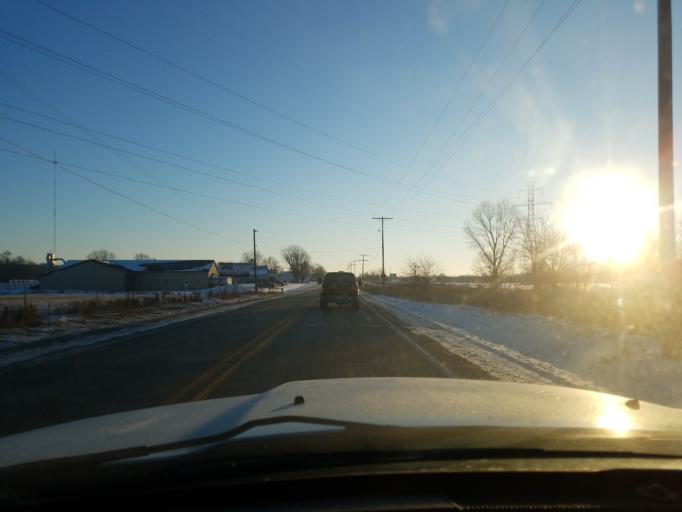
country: US
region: Indiana
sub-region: Marshall County
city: Bremen
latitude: 41.4472
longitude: -86.0831
